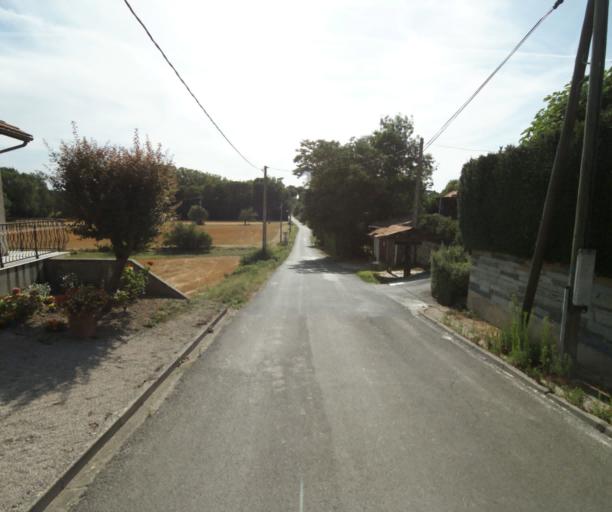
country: FR
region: Midi-Pyrenees
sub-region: Departement du Tarn
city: Soual
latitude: 43.5271
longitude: 2.0646
